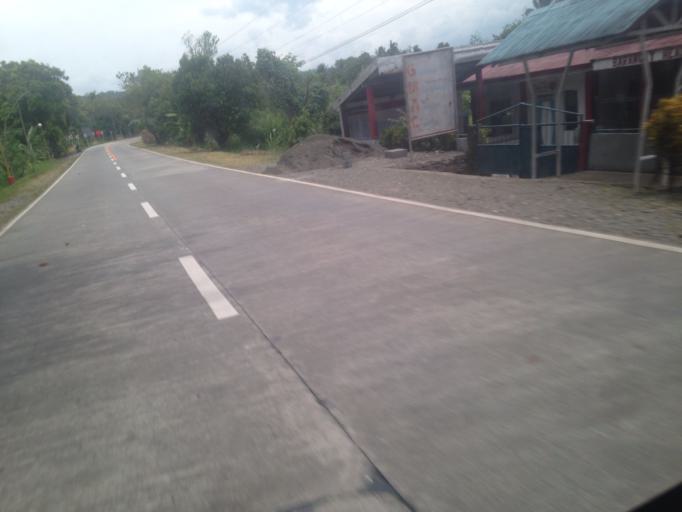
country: PH
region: Mimaropa
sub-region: Province of Mindoro Oriental
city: Saaban
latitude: 13.1097
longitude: 121.3112
